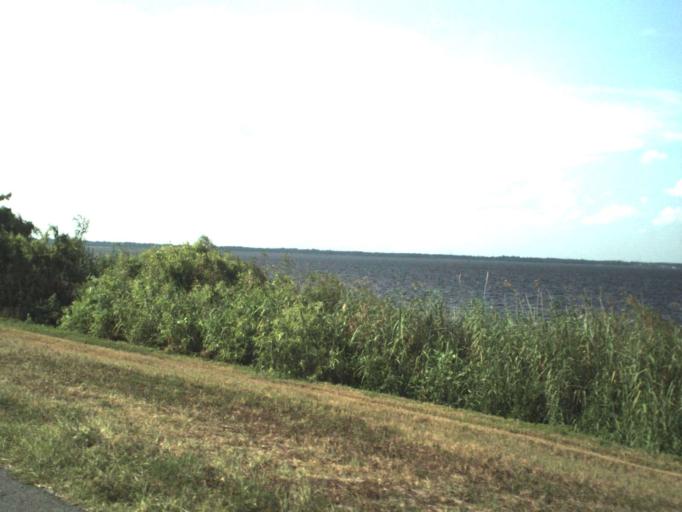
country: US
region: Florida
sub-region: Seminole County
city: Sanford
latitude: 28.8186
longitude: -81.2896
